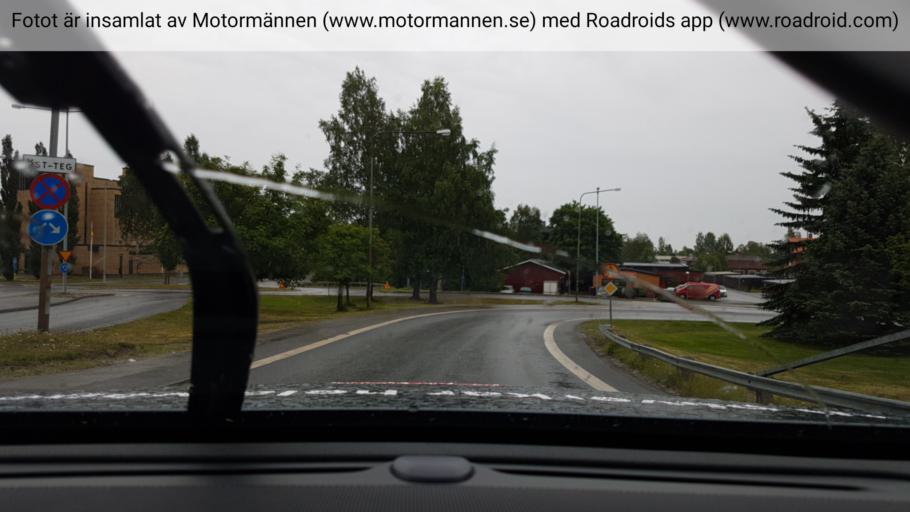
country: SE
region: Vaesterbotten
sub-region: Umea Kommun
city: Umea
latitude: 63.8199
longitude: 20.2513
